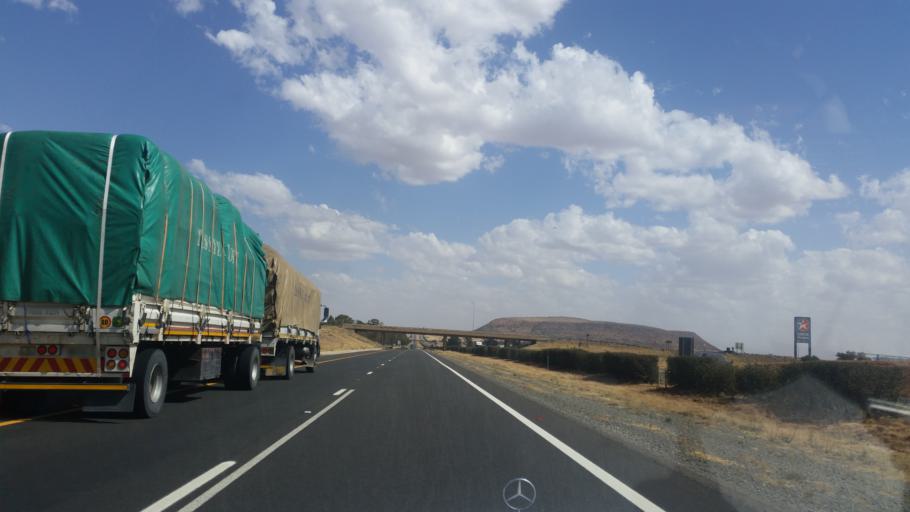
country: ZA
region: Orange Free State
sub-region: Mangaung Metropolitan Municipality
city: Bloemfontein
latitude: -29.1989
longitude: 26.1918
